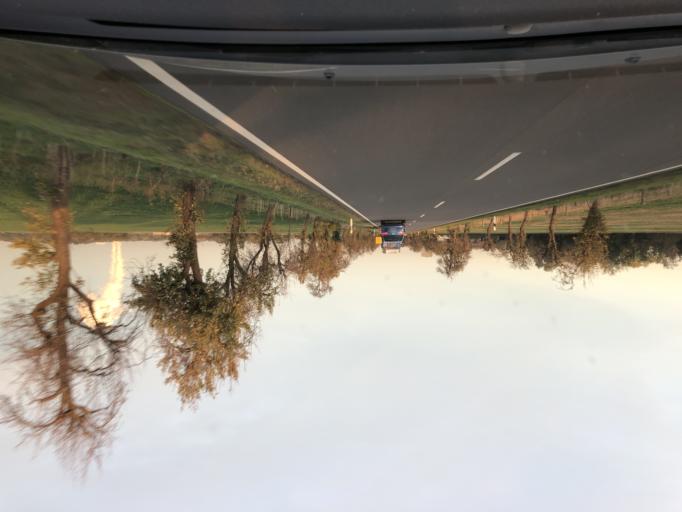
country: DE
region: Saxony
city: Elstertrebnitz
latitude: 51.1425
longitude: 12.2387
